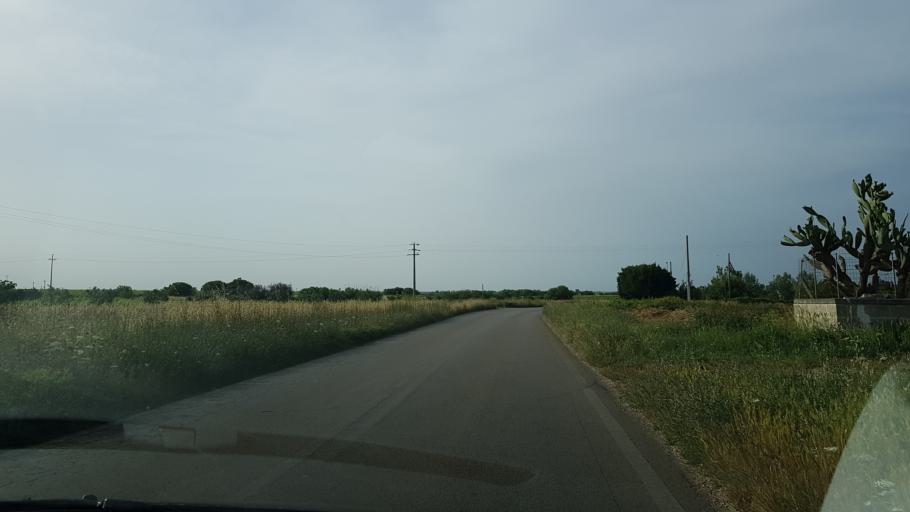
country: IT
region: Apulia
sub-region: Provincia di Brindisi
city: San Pancrazio Salentino
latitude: 40.3947
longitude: 17.8347
